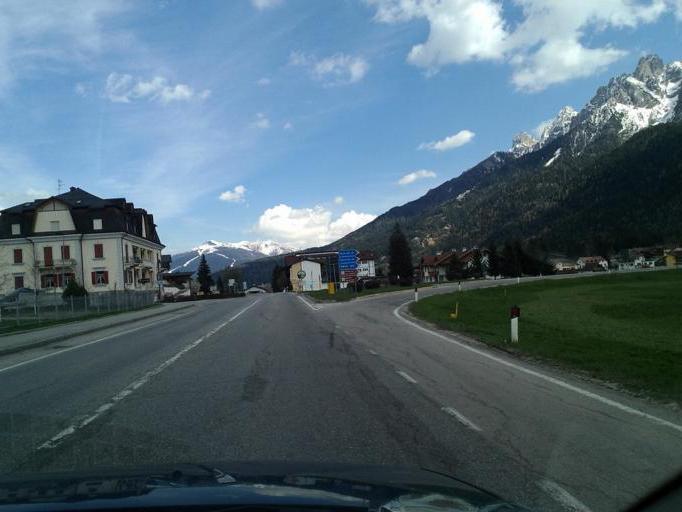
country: IT
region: Trentino-Alto Adige
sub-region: Bolzano
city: Dobbiaco
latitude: 46.7288
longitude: 12.2191
